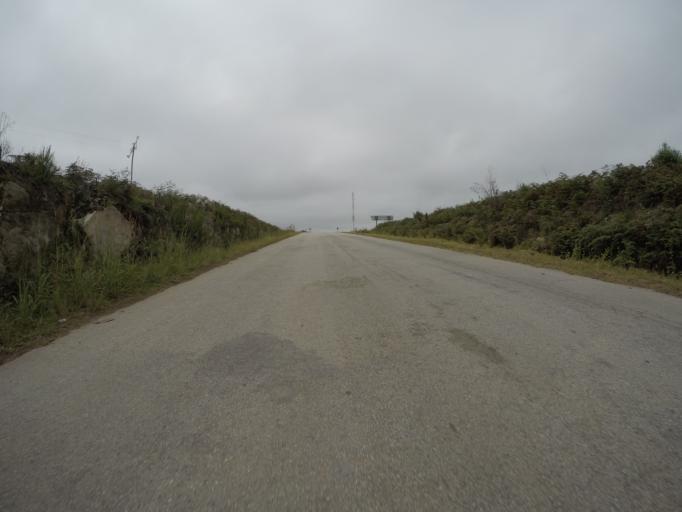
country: ZA
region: Eastern Cape
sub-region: Cacadu District Municipality
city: Kareedouw
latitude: -33.9817
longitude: 24.0509
